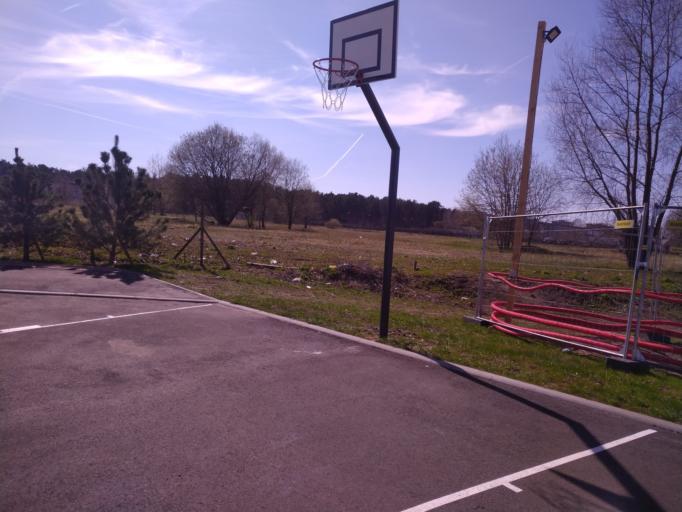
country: LV
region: Stopini
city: Ulbroka
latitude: 56.9385
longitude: 24.2233
